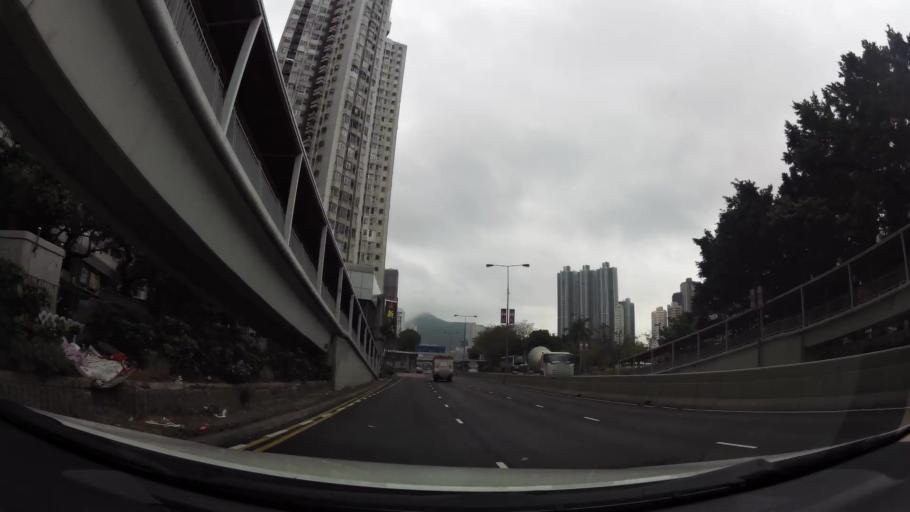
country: HK
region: Central and Western
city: Central
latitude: 22.2478
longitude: 114.1534
